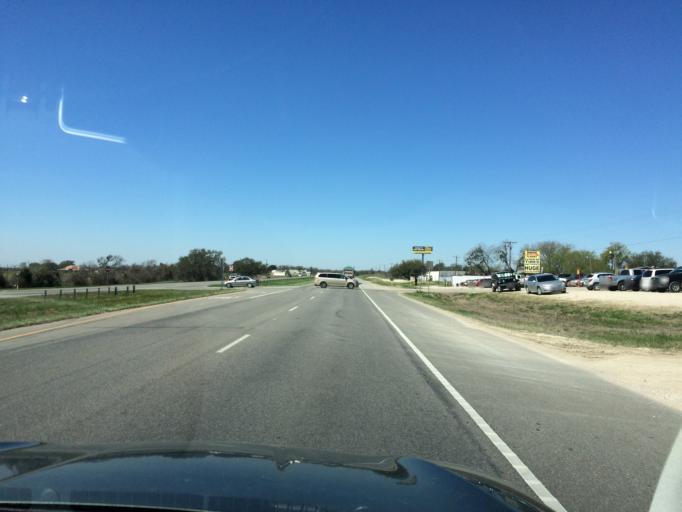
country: US
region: Texas
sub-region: Travis County
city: Garfield
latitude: 30.1880
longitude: -97.5644
